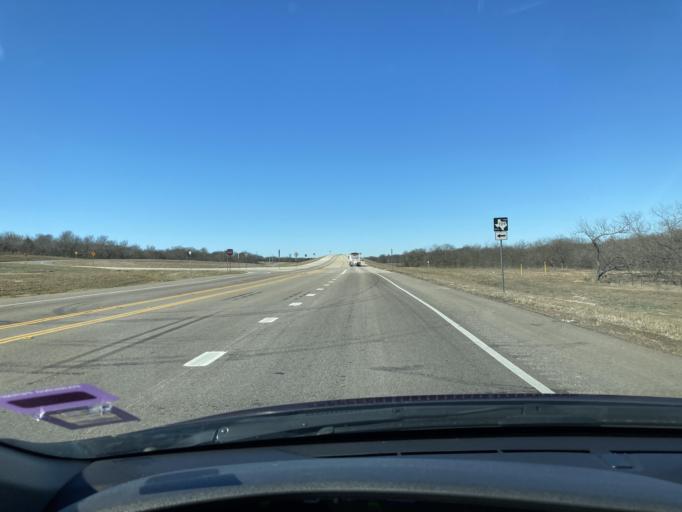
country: US
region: Texas
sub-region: Navarro County
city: Corsicana
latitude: 32.0444
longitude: -96.4661
